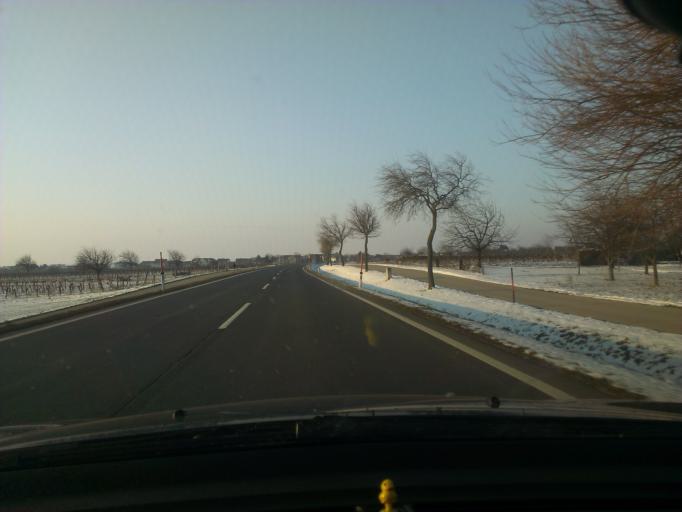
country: AT
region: Burgenland
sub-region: Eisenstadt-Umgebung
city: Donnerskirchen
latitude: 47.9001
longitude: 16.6528
